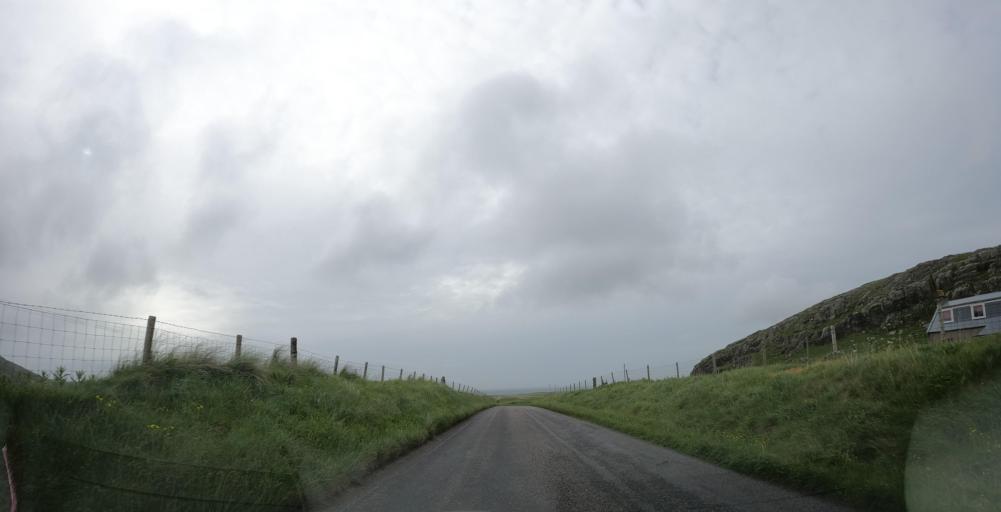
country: GB
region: Scotland
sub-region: Eilean Siar
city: Barra
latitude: 56.9681
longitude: -7.5155
